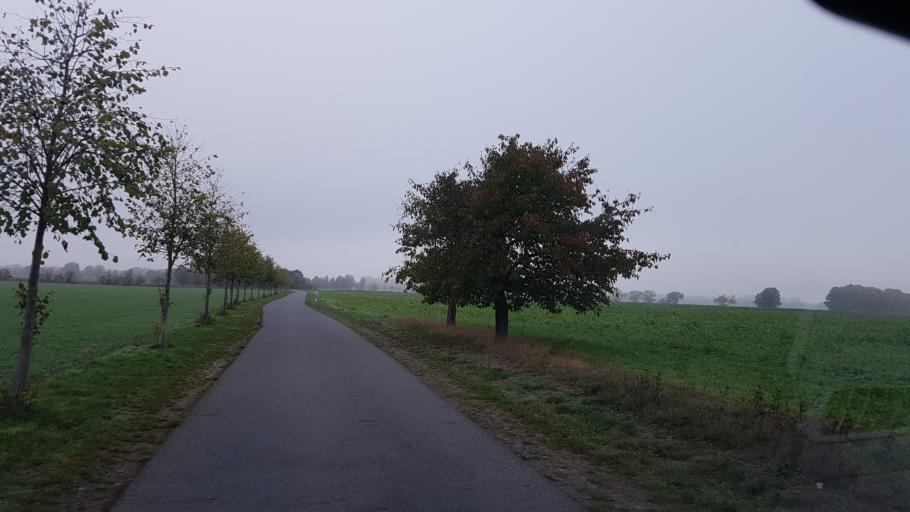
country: DE
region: Brandenburg
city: Schonewalde
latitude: 51.6770
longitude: 13.6221
